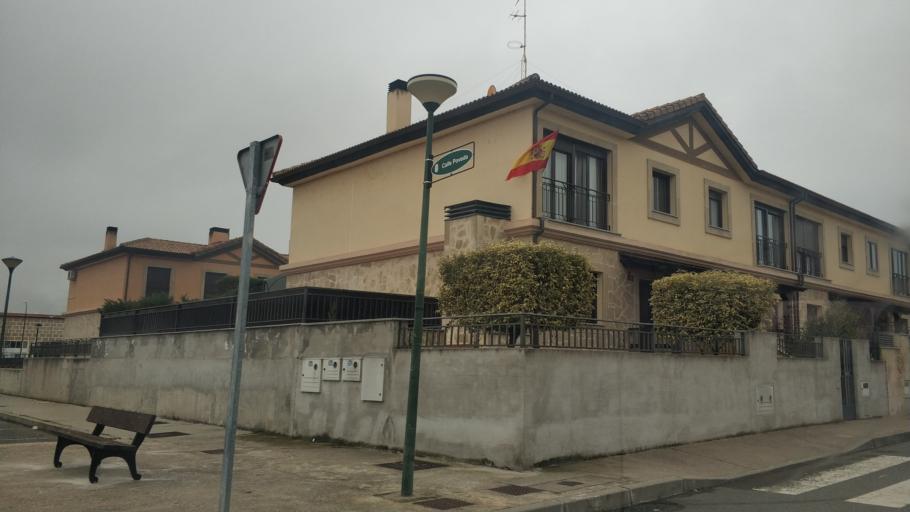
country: ES
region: Castille and Leon
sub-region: Provincia de Salamanca
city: Villamayor
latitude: 40.9963
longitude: -5.7227
